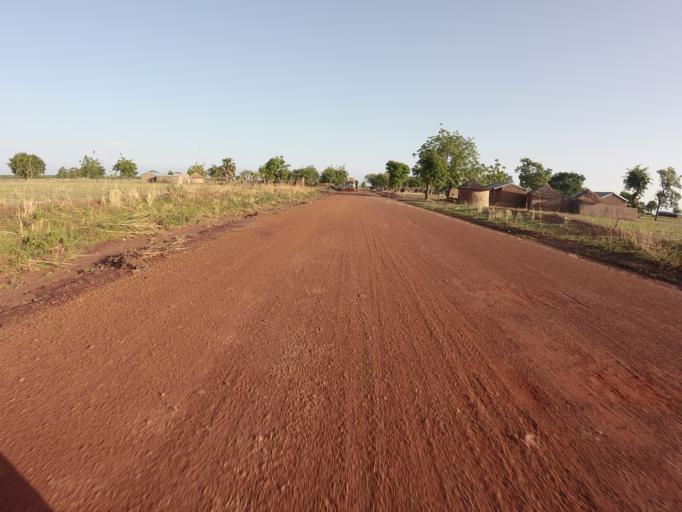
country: TG
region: Savanes
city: Sansanne-Mango
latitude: 10.3569
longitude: -0.0933
